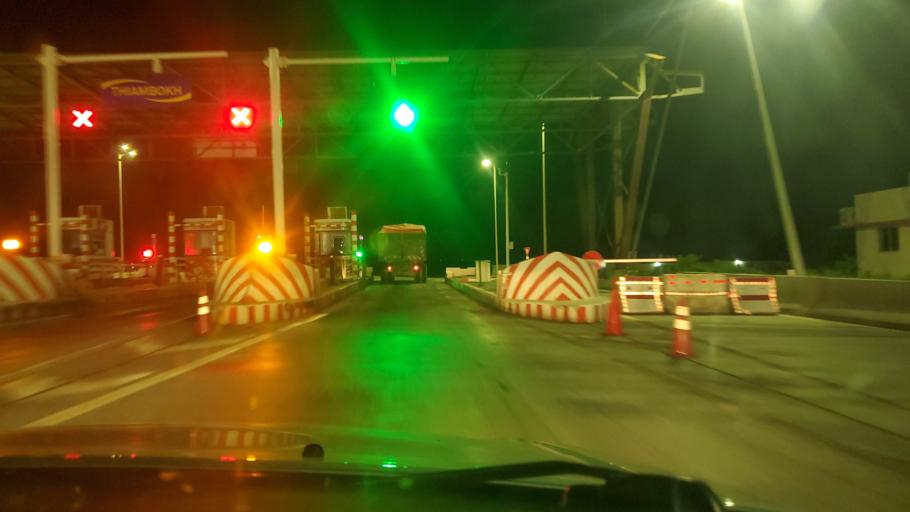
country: SN
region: Thies
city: Pout
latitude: 14.6978
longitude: -17.0409
